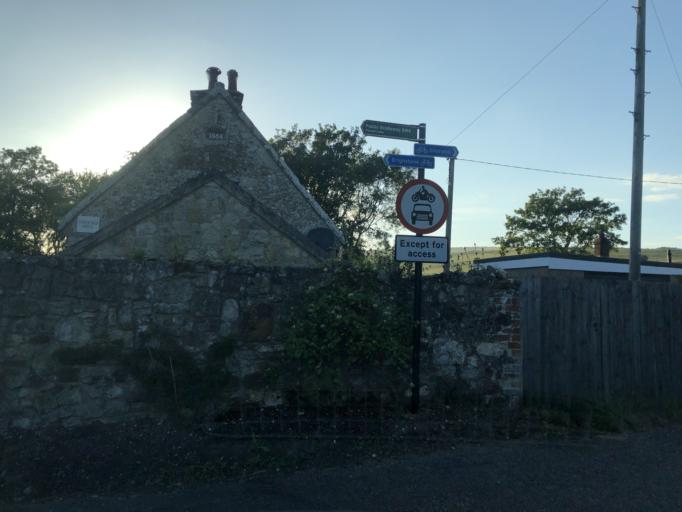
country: GB
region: England
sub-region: Isle of Wight
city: Chale
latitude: 50.6417
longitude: -1.3572
